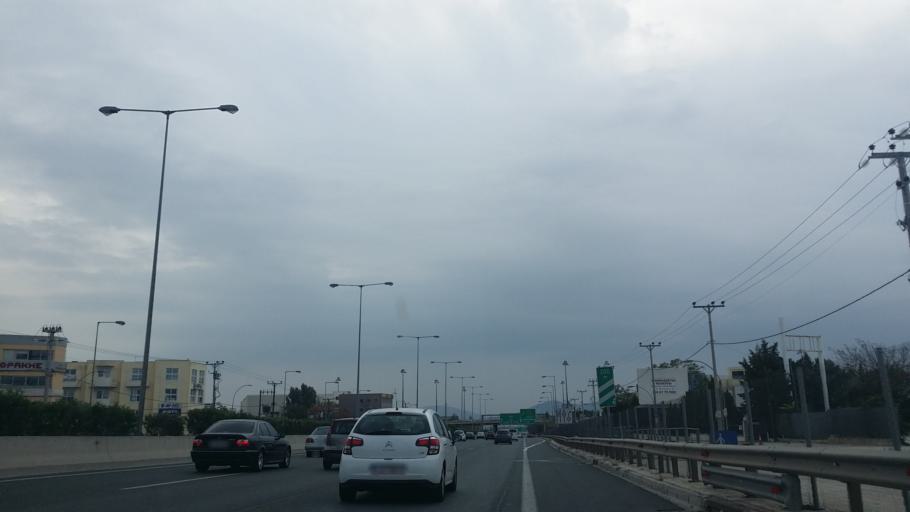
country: GR
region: Attica
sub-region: Nomarchia Athinas
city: Metamorfosi
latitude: 38.0705
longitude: 23.7640
